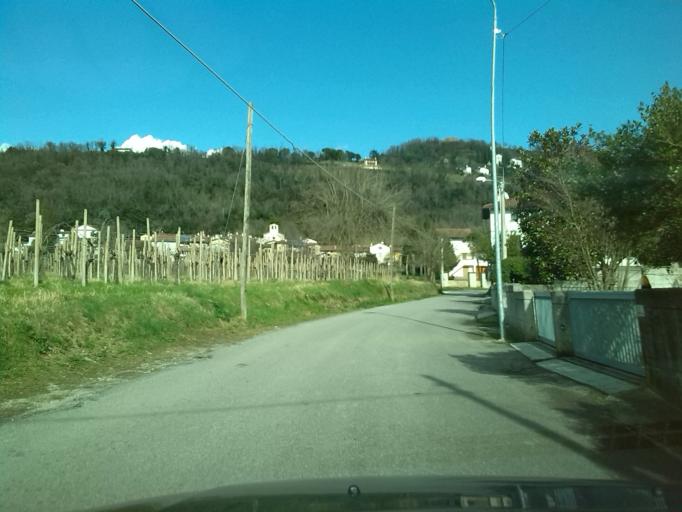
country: IT
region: Friuli Venezia Giulia
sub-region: Provincia di Gorizia
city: Cormons
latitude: 45.9634
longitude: 13.4663
